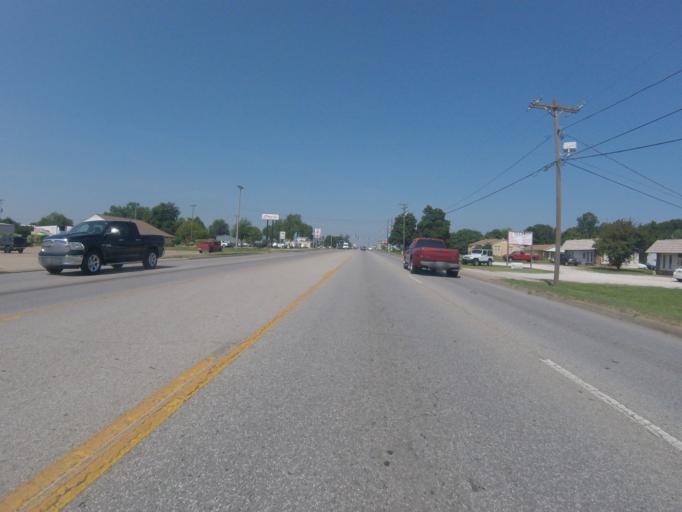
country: US
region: Arkansas
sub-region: Washington County
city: Springdale
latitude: 36.1671
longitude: -94.1239
